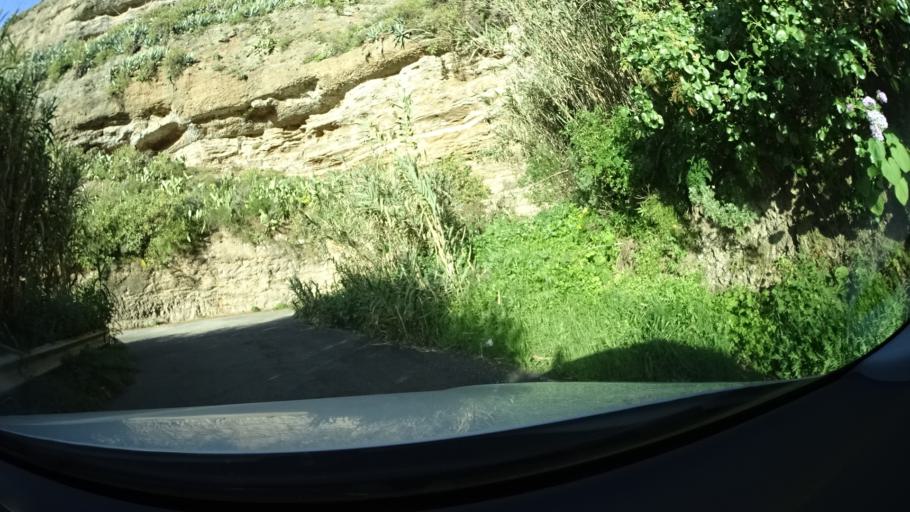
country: ES
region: Canary Islands
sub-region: Provincia de Las Palmas
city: Artenara
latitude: 28.0481
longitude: -15.6658
